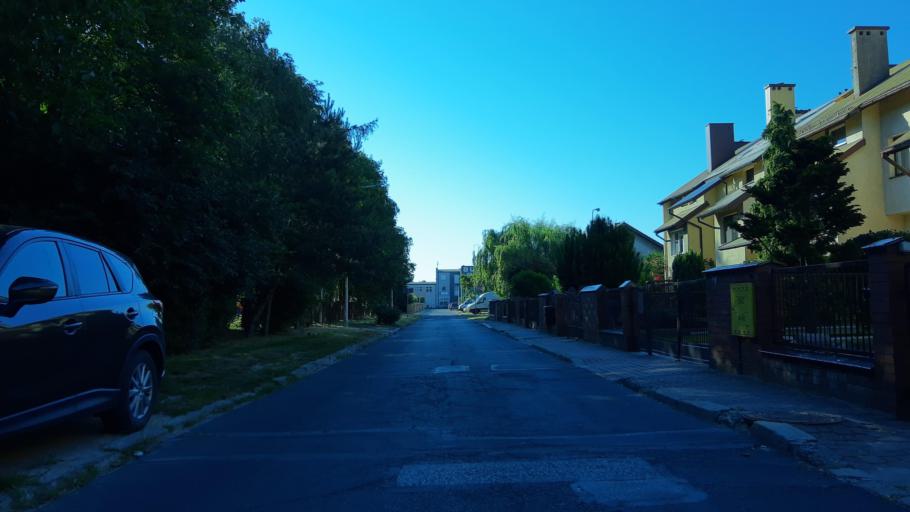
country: PL
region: Lodz Voivodeship
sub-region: Powiat sieradzki
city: Sieradz
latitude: 51.5863
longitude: 18.7168
